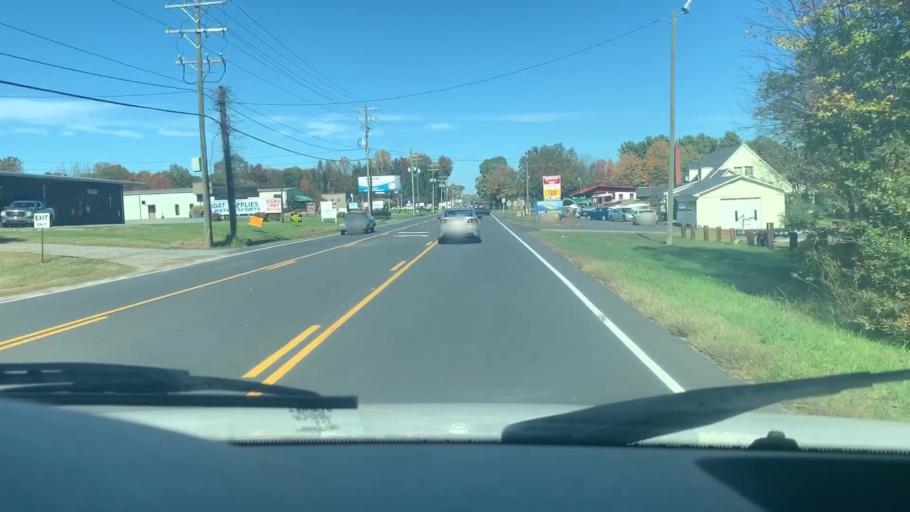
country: US
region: North Carolina
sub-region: Lincoln County
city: Lowesville
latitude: 35.4579
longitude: -80.9922
